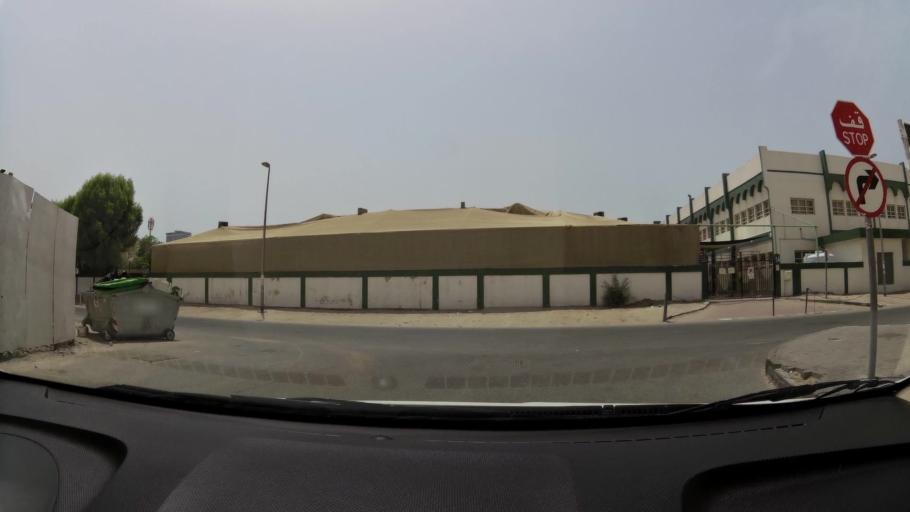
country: AE
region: Ash Shariqah
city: Sharjah
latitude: 25.3488
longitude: 55.4023
